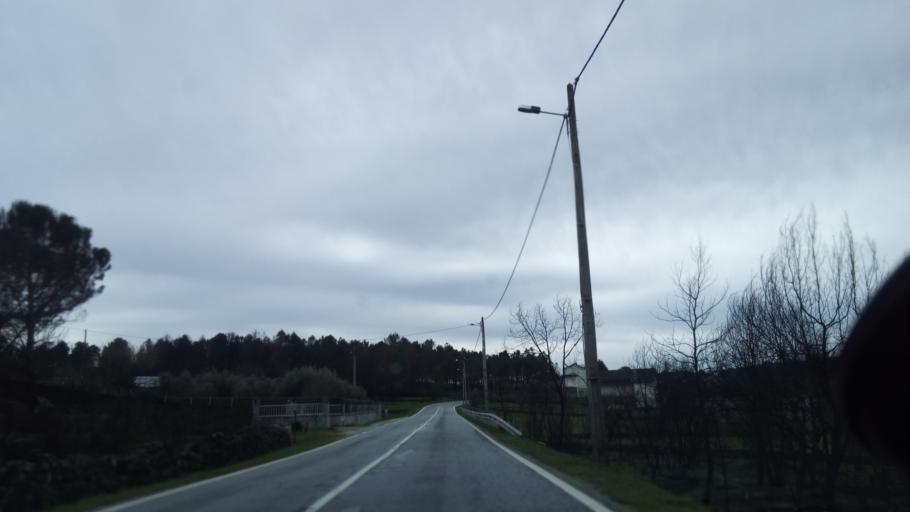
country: PT
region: Guarda
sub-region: Seia
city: Seia
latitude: 40.5017
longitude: -7.6513
